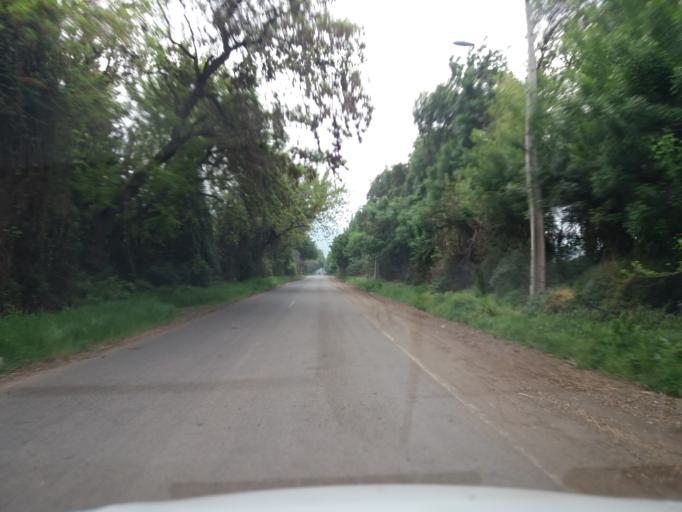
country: CL
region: Valparaiso
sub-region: Provincia de Quillota
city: Hacienda La Calera
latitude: -32.8555
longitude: -71.1040
